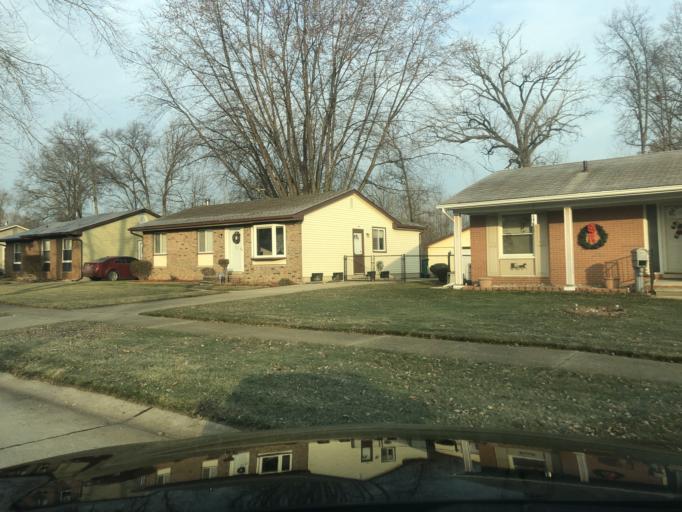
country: US
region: Michigan
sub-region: Wayne County
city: Romulus
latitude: 42.1913
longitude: -83.3312
